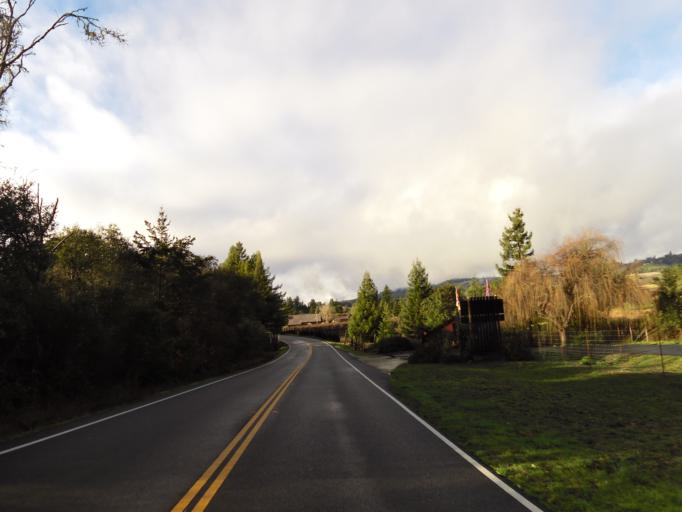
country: US
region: California
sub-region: Mendocino County
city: Boonville
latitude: 39.0982
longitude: -123.4855
